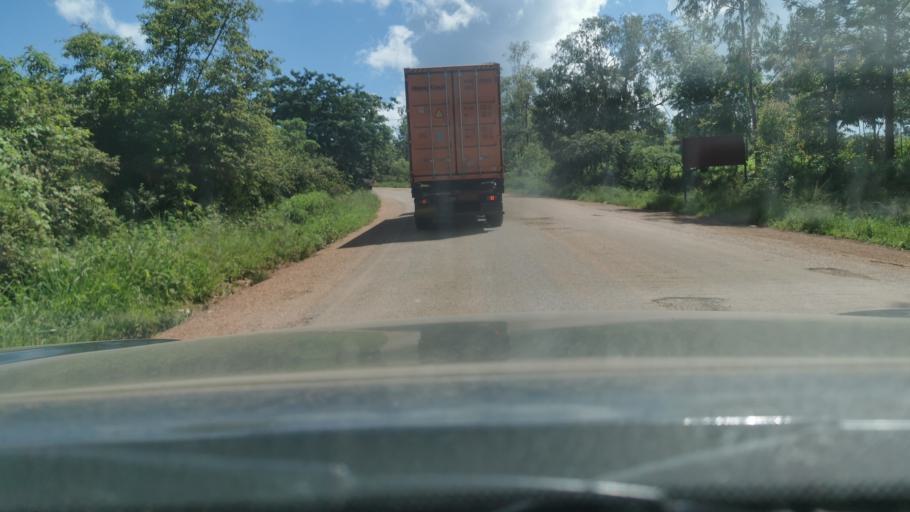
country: TZ
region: Kagera
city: Ngara
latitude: -2.3839
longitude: 30.7896
